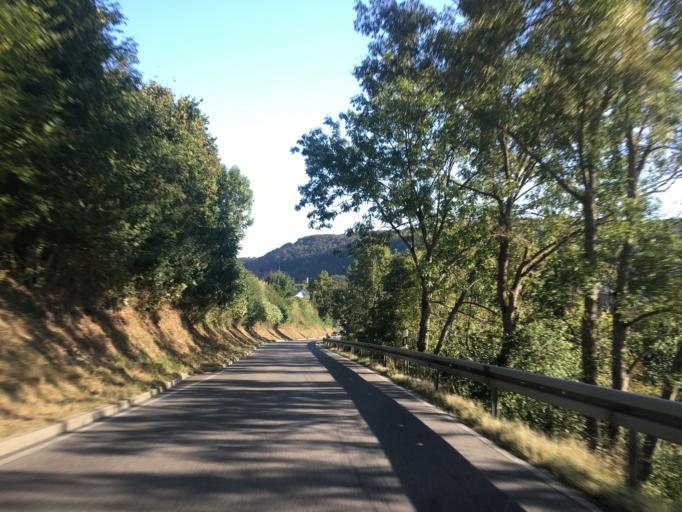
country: DE
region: Baden-Wuerttemberg
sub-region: Tuebingen Region
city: Zwiefalten
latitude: 48.2362
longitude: 9.4609
